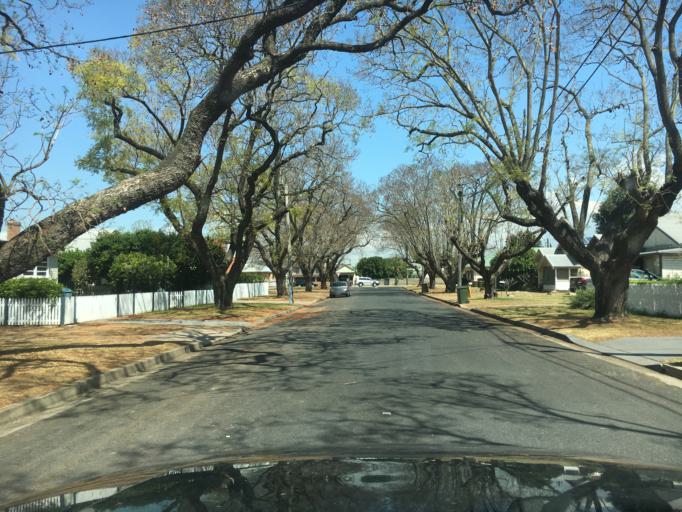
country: AU
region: New South Wales
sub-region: Singleton
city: Singleton
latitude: -32.5712
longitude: 151.1700
